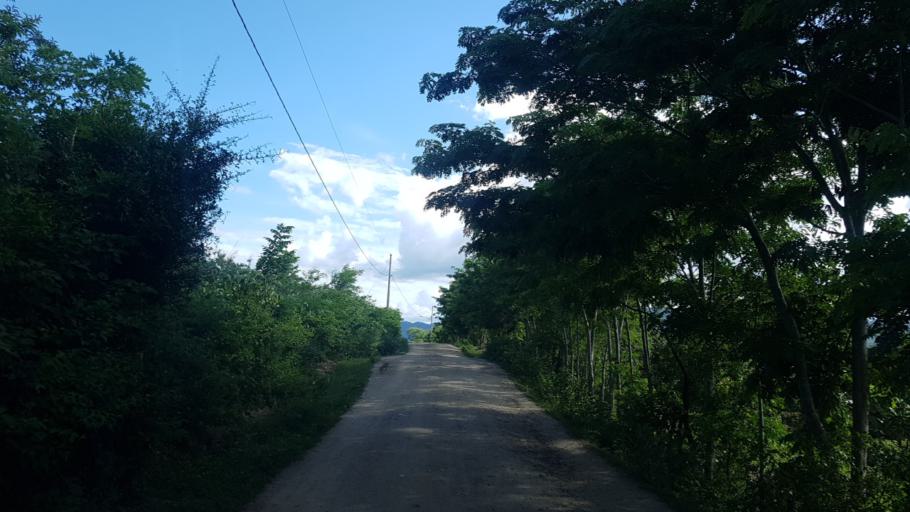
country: NI
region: Nueva Segovia
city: Mozonte
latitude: 13.6464
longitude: -86.3984
